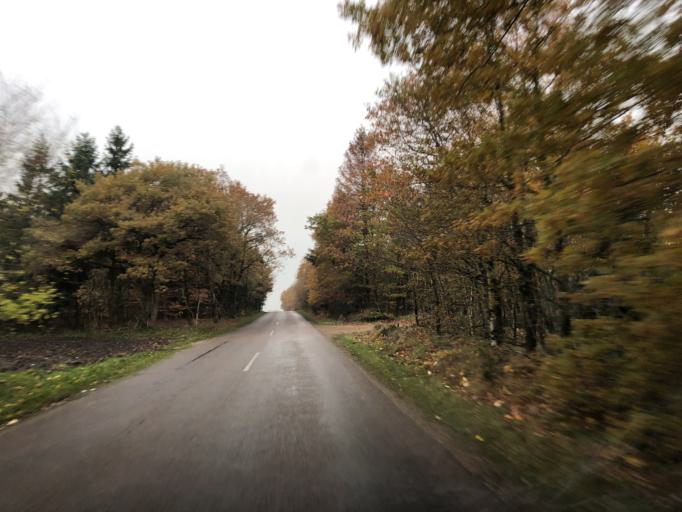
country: DK
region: Central Jutland
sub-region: Herning Kommune
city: Avlum
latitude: 56.2475
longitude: 8.8640
